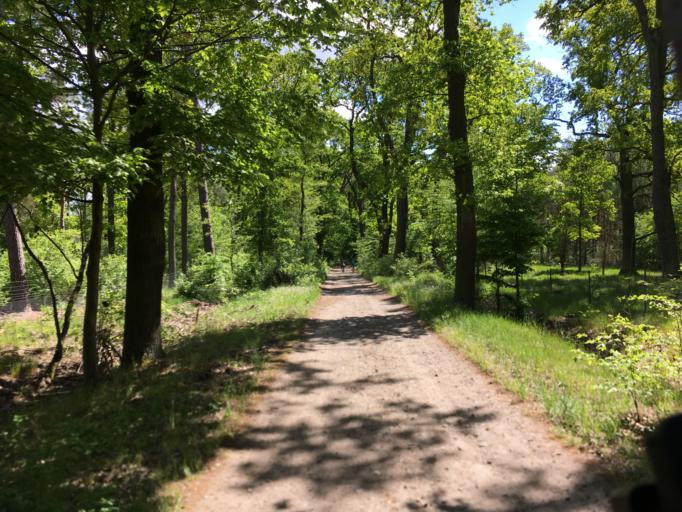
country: DE
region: Brandenburg
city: Trebbin
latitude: 52.1717
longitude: 13.2183
